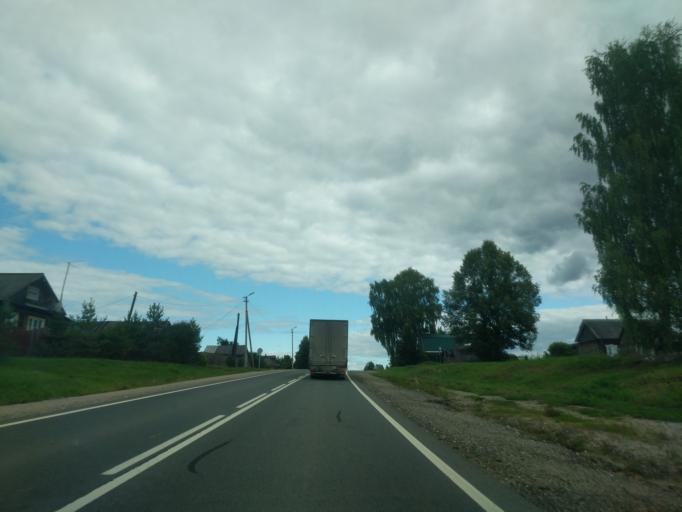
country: RU
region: Kostroma
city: Ostrovskoye
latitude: 57.8222
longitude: 42.1940
